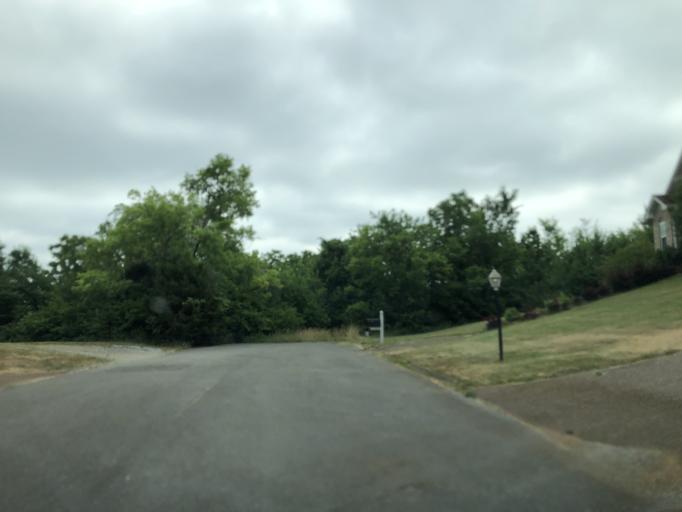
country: US
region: Tennessee
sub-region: Davidson County
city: Goodlettsville
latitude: 36.2963
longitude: -86.7371
